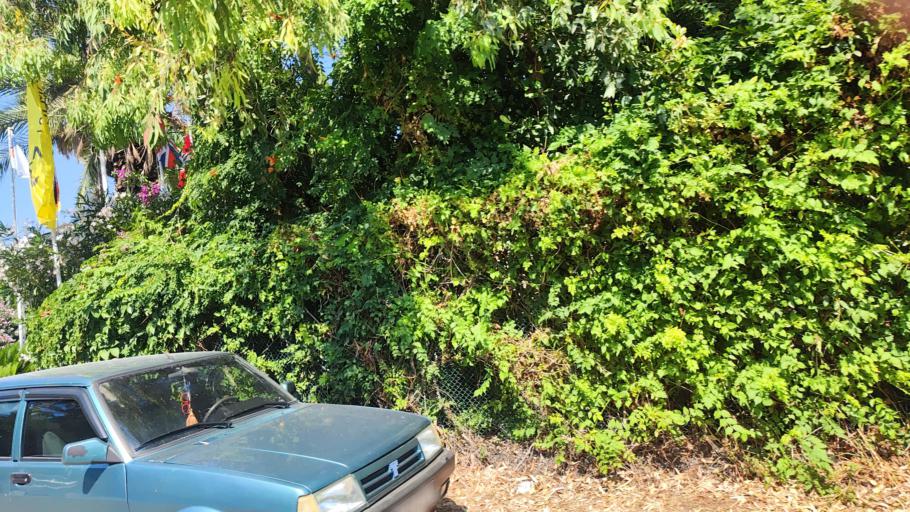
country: TR
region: Mugla
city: Sarigerme
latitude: 36.7044
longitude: 28.6963
